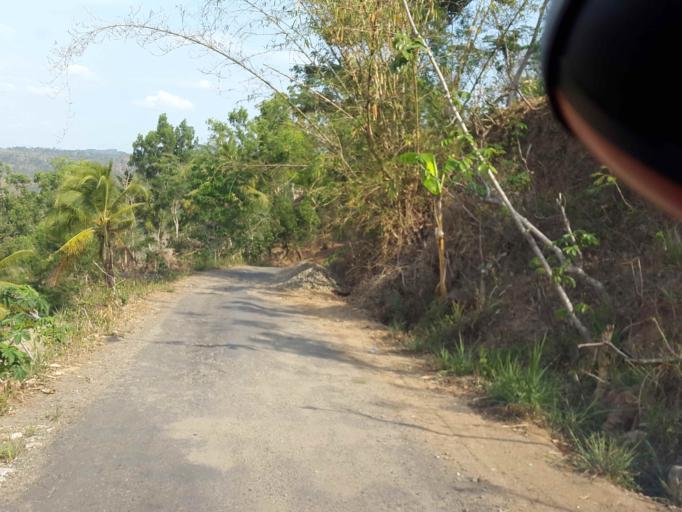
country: ID
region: East Java
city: Krajan
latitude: -8.0966
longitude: 111.0261
